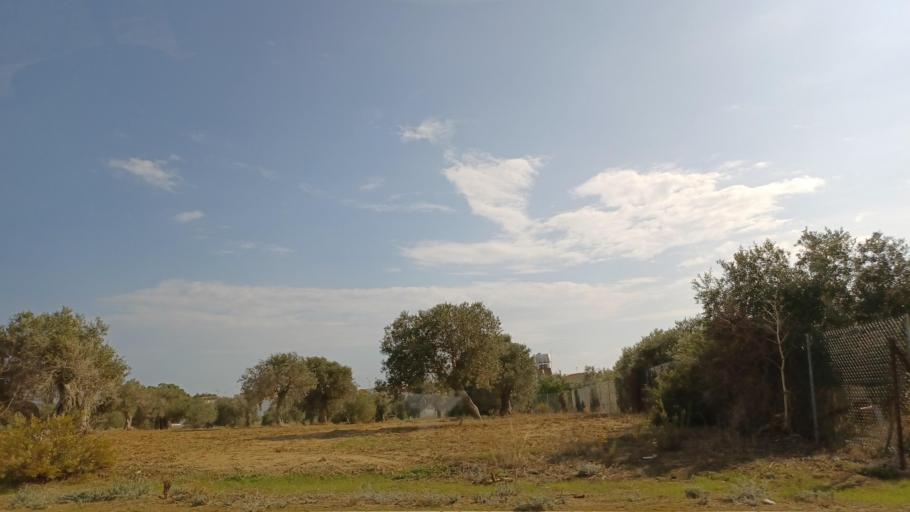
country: CY
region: Larnaka
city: Tersefanou
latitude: 34.7865
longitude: 33.4951
